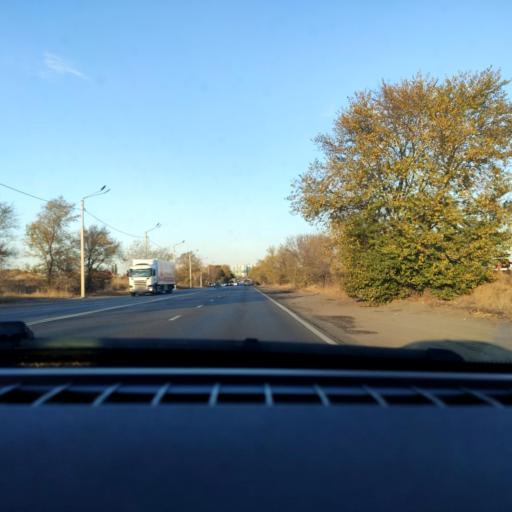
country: RU
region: Voronezj
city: Maslovka
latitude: 51.6232
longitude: 39.2787
